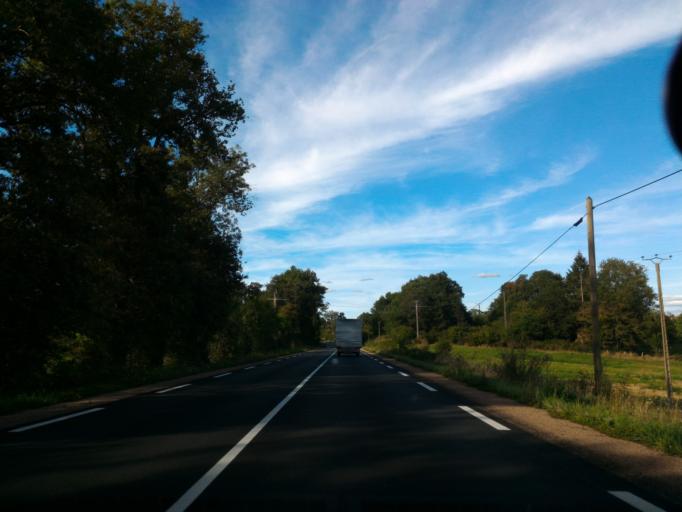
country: FR
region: Limousin
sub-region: Departement de la Haute-Vienne
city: Magnac-Laval
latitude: 46.1570
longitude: 1.1304
